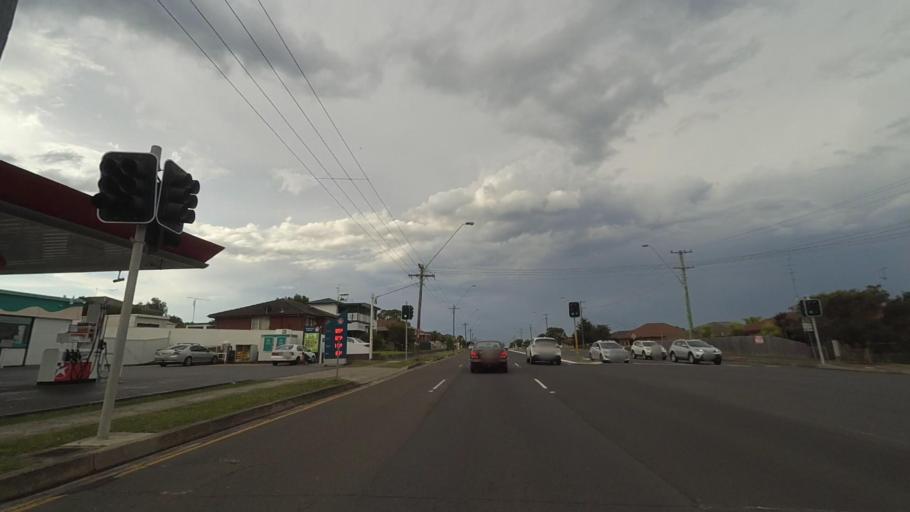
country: AU
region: New South Wales
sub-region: Shellharbour
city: Barrack Heights
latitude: -34.5649
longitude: 150.8601
